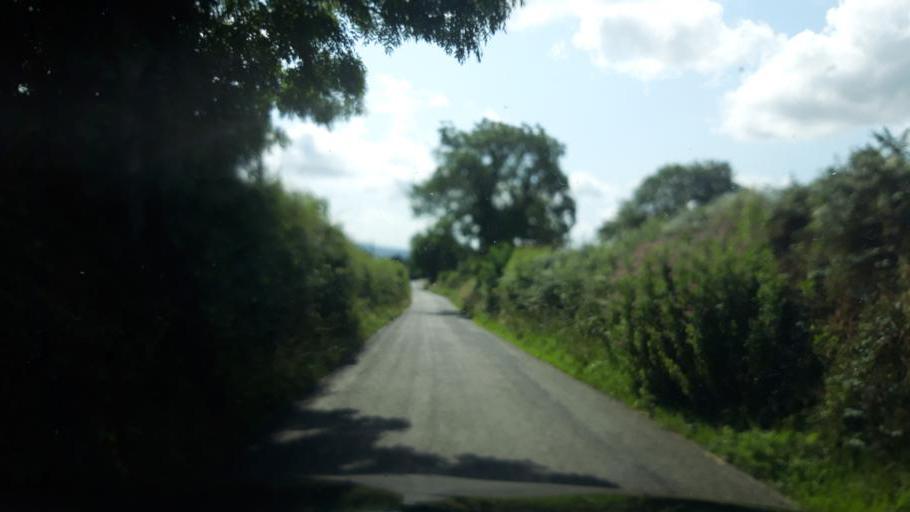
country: IE
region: Leinster
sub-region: Kilkenny
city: Graiguenamanagh
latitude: 52.5550
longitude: -6.9779
